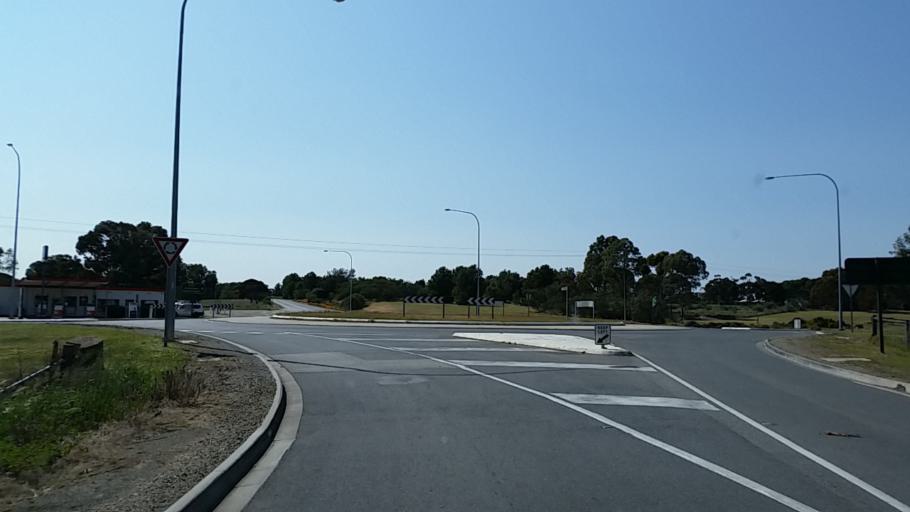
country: AU
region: South Australia
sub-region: Port Pirie City and Dists
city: Crystal Brook
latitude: -33.2649
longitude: 138.3452
